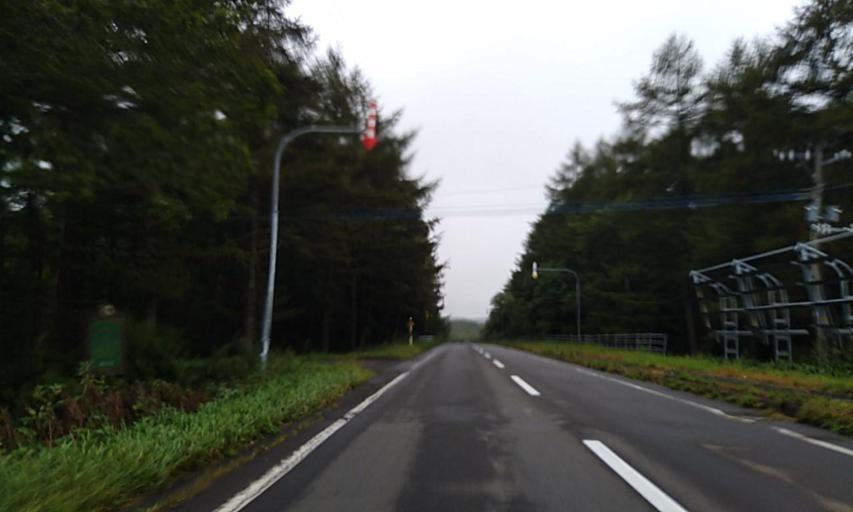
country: JP
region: Hokkaido
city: Shibetsu
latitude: 43.4911
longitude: 144.6413
